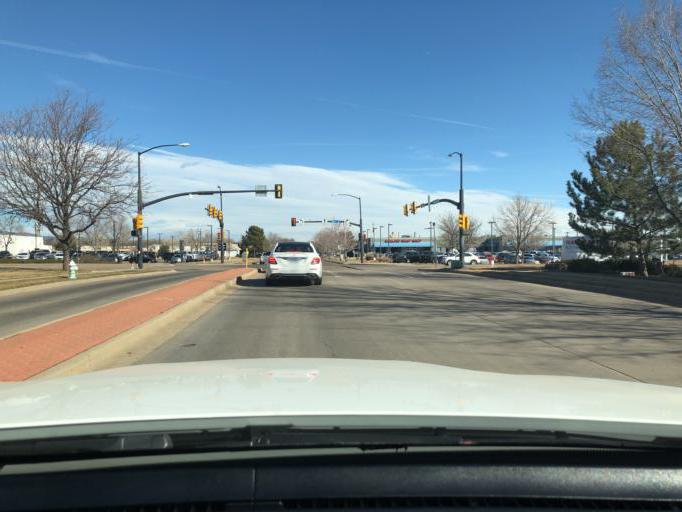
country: US
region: Colorado
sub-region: Boulder County
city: Boulder
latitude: 40.0215
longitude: -105.2385
